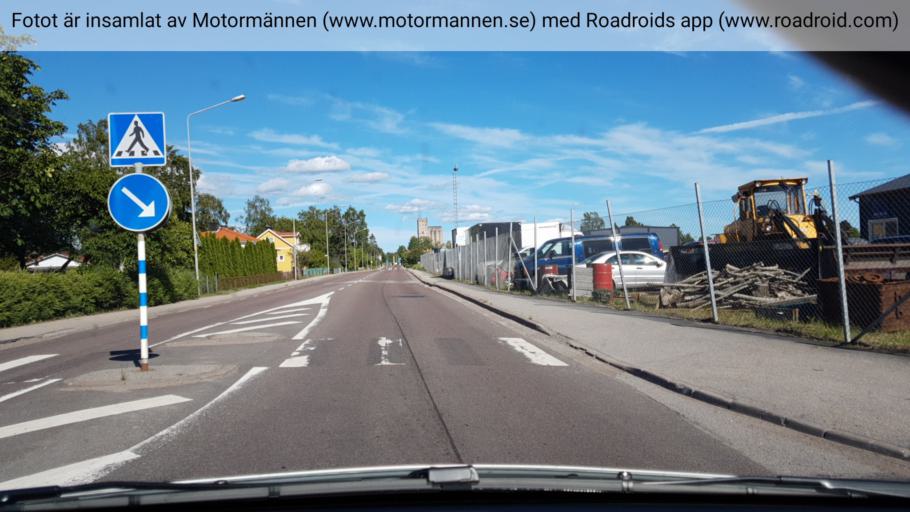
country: SE
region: Vaestra Goetaland
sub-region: Toreboda Kommun
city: Toereboda
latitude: 58.7047
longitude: 14.1149
